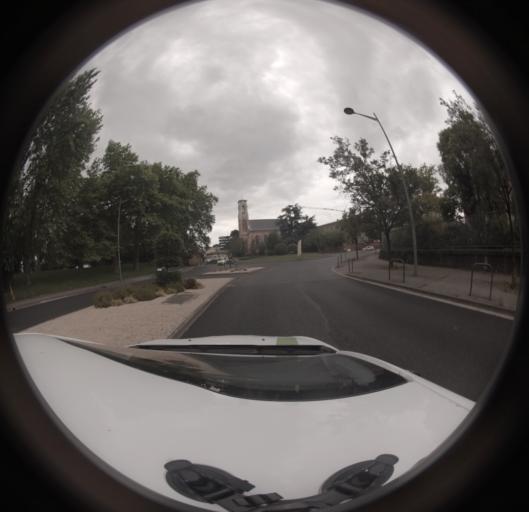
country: FR
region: Midi-Pyrenees
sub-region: Departement du Tarn-et-Garonne
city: Montauban
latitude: 44.0095
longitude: 1.3593
